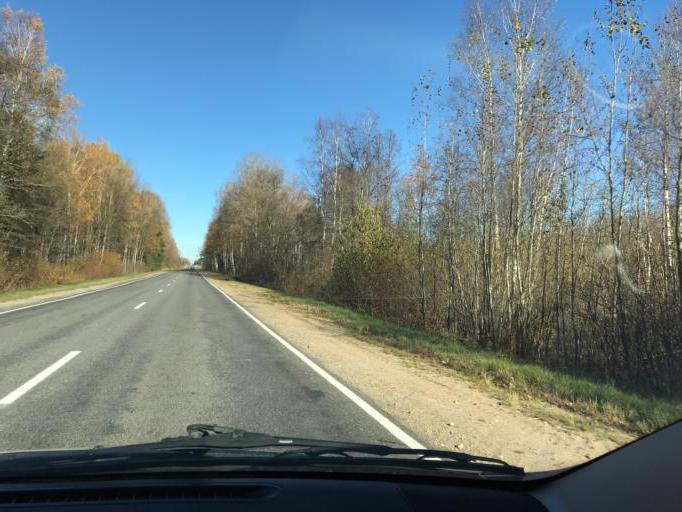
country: BY
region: Vitebsk
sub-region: Ushatski Rayon
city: Ushachy
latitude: 55.0766
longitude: 28.7548
